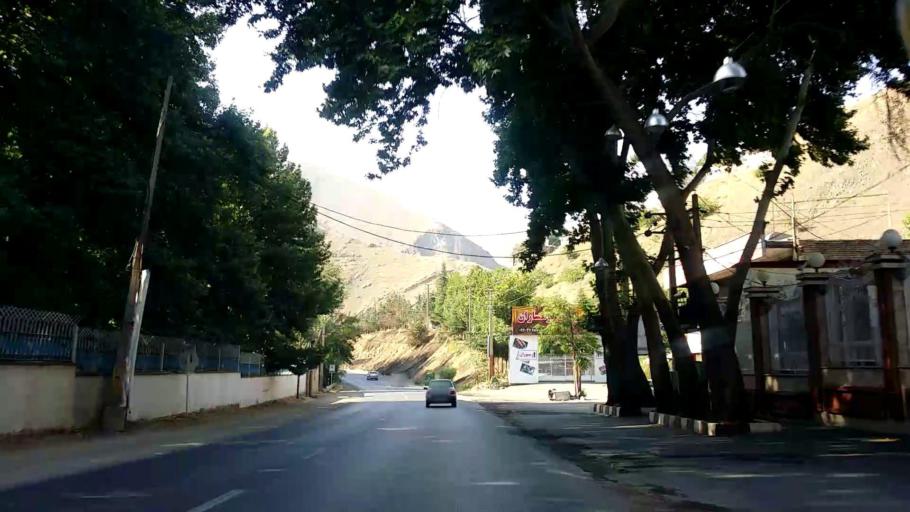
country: IR
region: Alborz
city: Karaj
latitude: 35.8542
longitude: 51.0591
